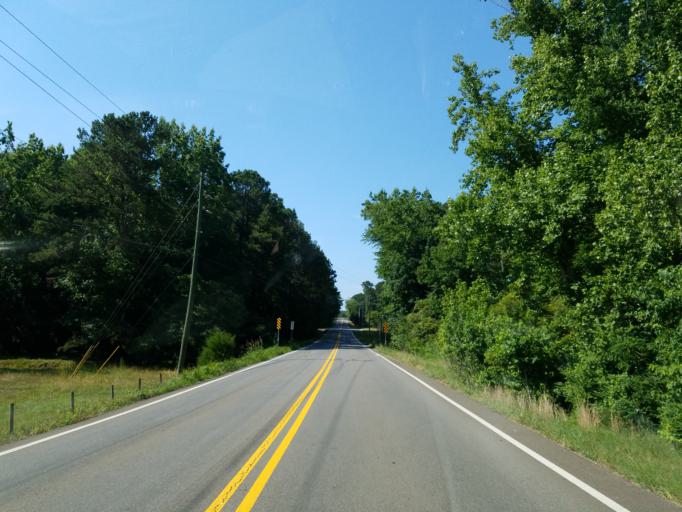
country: US
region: Georgia
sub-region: Fulton County
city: Milton
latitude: 34.2081
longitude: -84.2894
